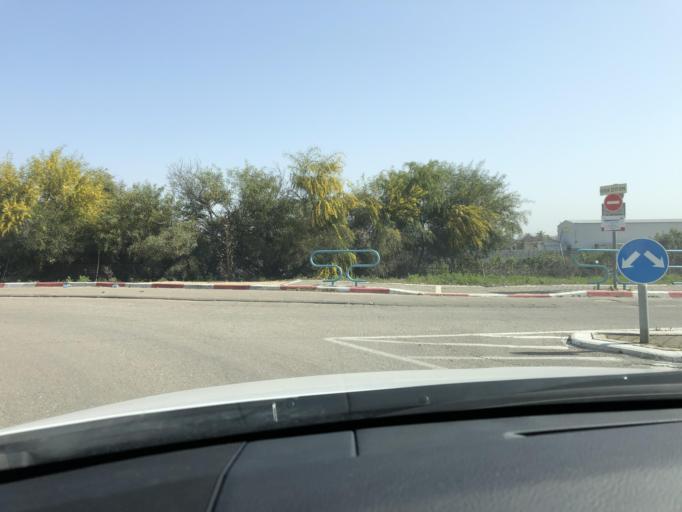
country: IL
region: Central District
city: Hod HaSharon
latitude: 32.1346
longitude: 34.9119
